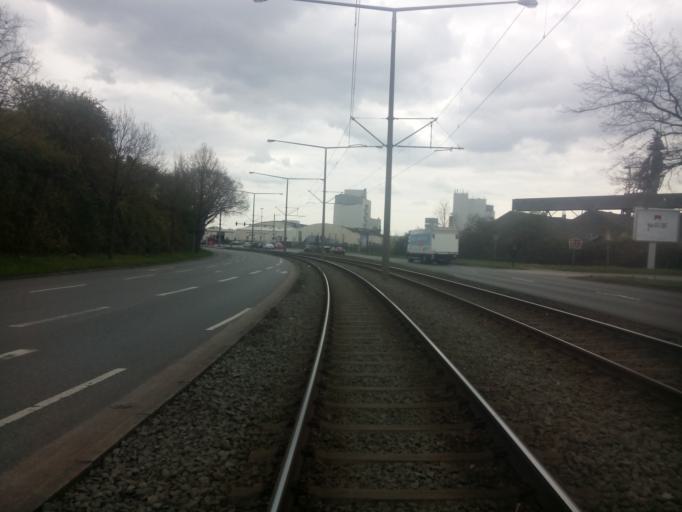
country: DE
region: Bremen
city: Bremen
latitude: 53.1111
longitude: 8.7543
